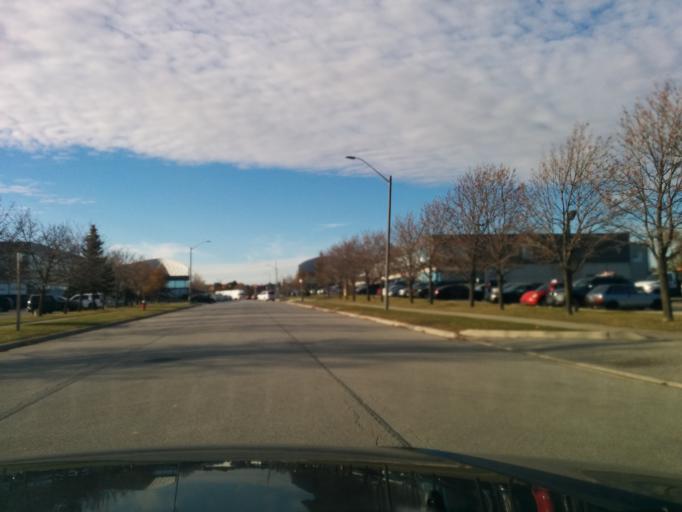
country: CA
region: Ontario
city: Etobicoke
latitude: 43.6127
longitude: -79.5757
